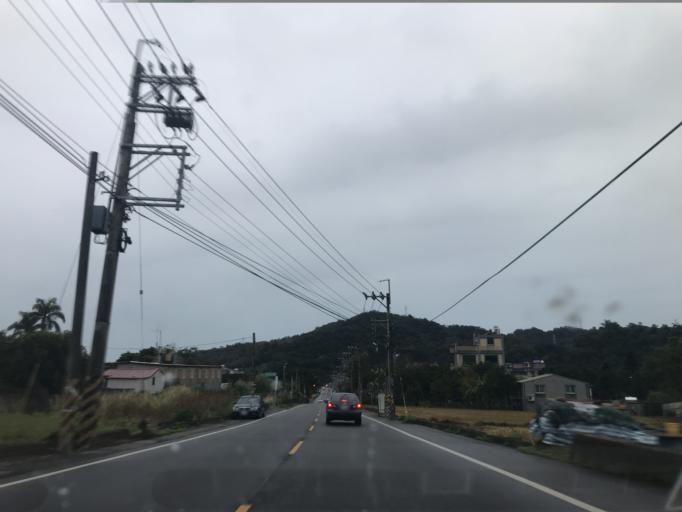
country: TW
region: Taiwan
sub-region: Hsinchu
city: Zhubei
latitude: 24.8390
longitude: 121.1054
